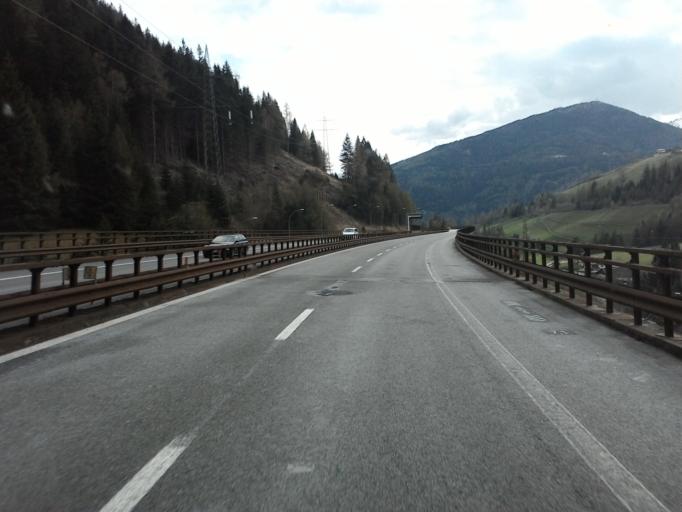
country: IT
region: Trentino-Alto Adige
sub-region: Bolzano
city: Colle Isarco
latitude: 46.9548
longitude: 11.4557
